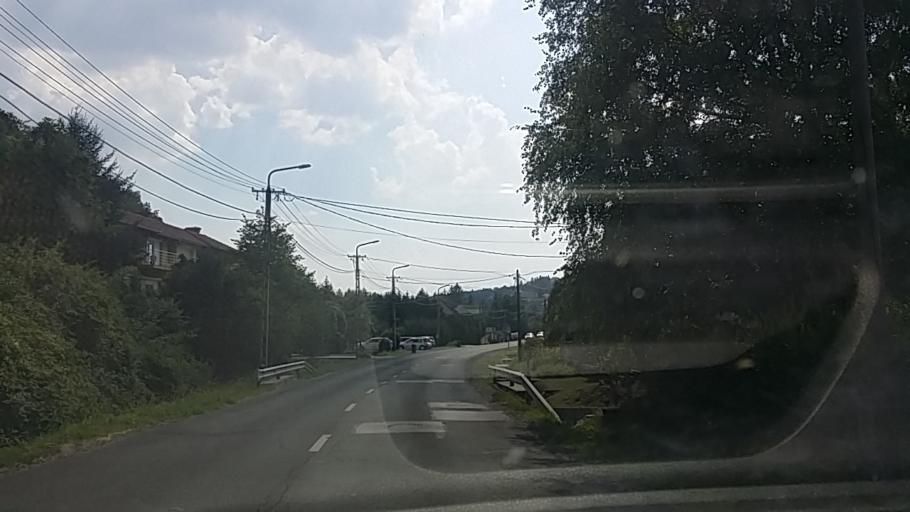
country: HU
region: Baranya
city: Pecs
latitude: 46.0790
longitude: 18.1900
